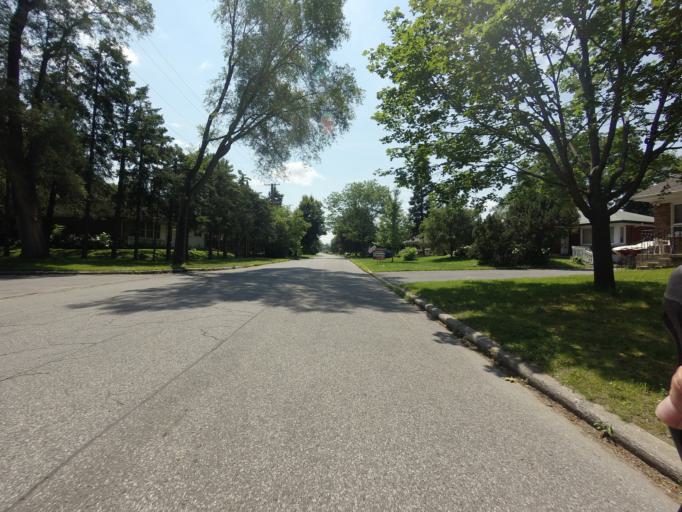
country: CA
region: Ontario
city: Ottawa
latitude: 45.3854
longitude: -75.6701
